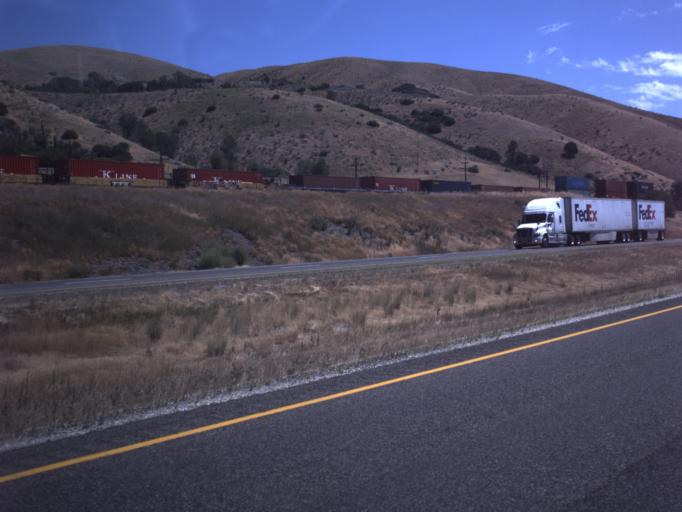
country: US
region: Utah
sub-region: Summit County
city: Coalville
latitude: 41.0039
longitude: -111.4734
